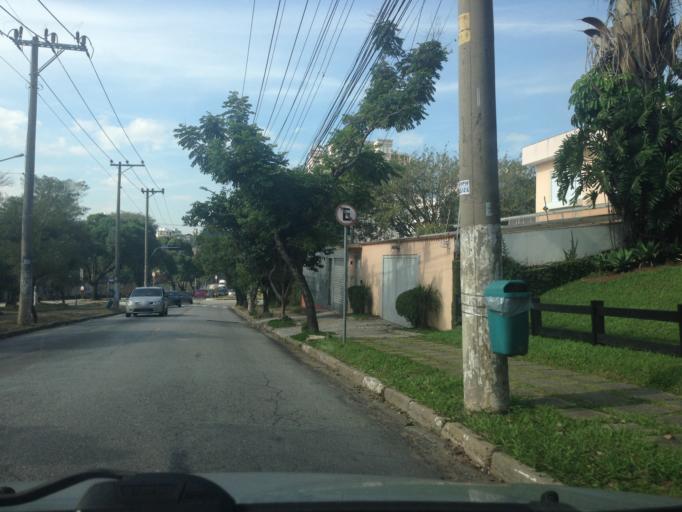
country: BR
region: Sao Paulo
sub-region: Osasco
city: Osasco
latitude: -23.5209
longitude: -46.7133
